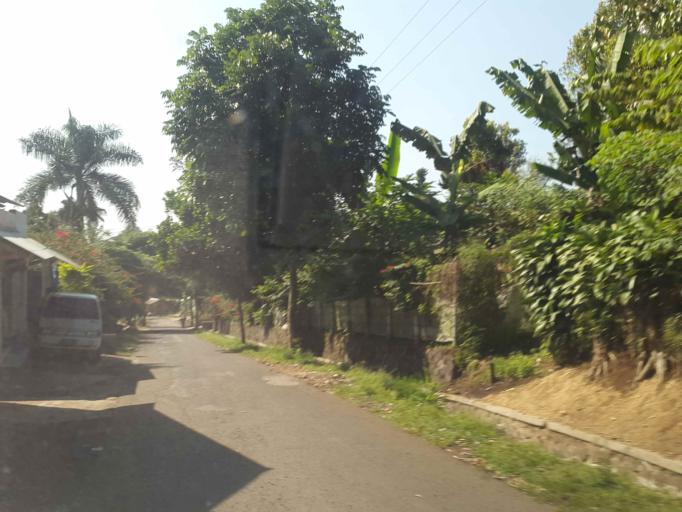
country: ID
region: West Java
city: Sukabumi
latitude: -6.8345
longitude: 107.0603
